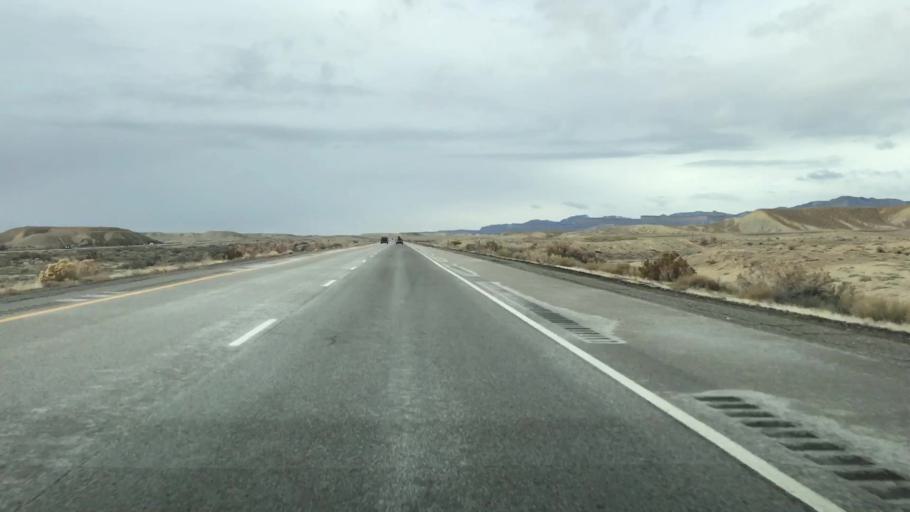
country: US
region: Utah
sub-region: Grand County
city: Moab
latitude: 38.9412
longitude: -109.5130
